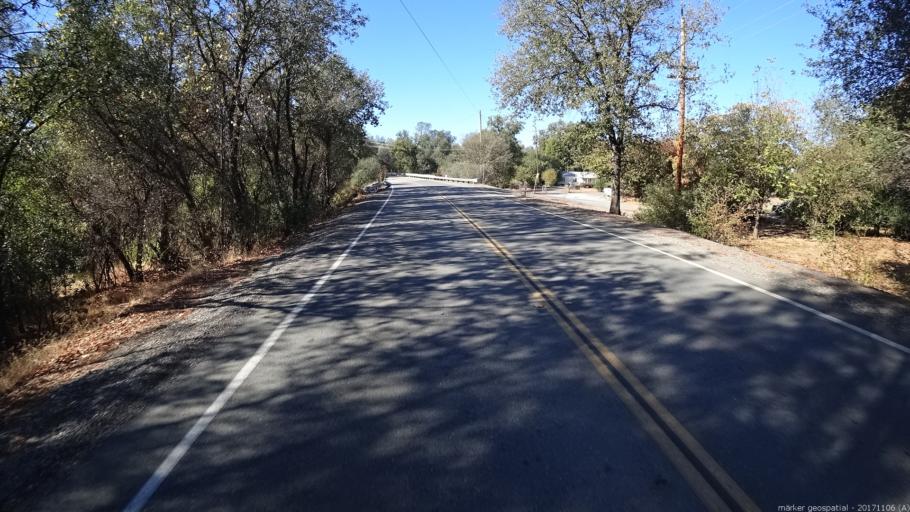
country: US
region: California
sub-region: Shasta County
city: Palo Cedro
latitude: 40.5890
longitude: -122.3044
